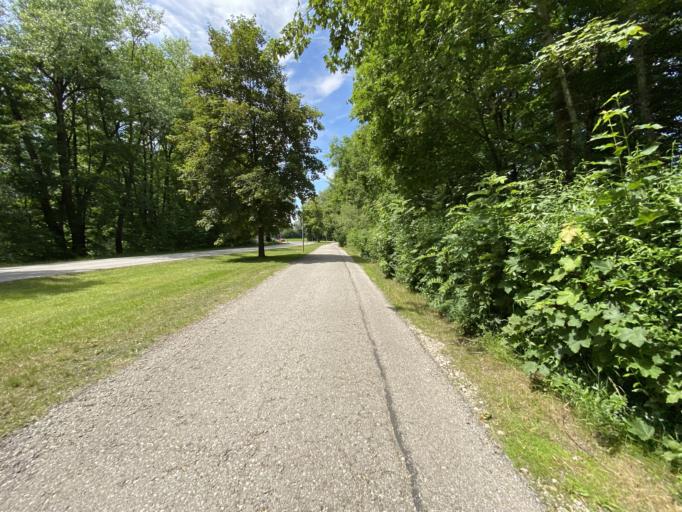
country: DE
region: Bavaria
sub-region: Upper Bavaria
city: Gilching
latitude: 48.1077
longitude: 11.3161
